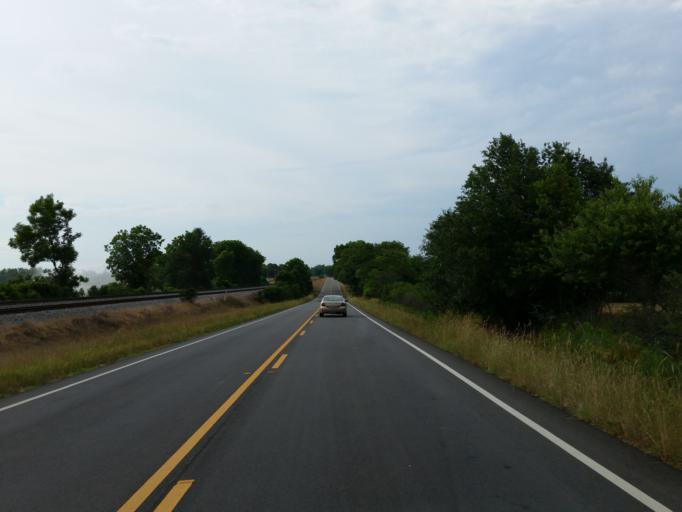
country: US
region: Georgia
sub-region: Turner County
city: Ashburn
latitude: 31.6386
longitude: -83.6166
